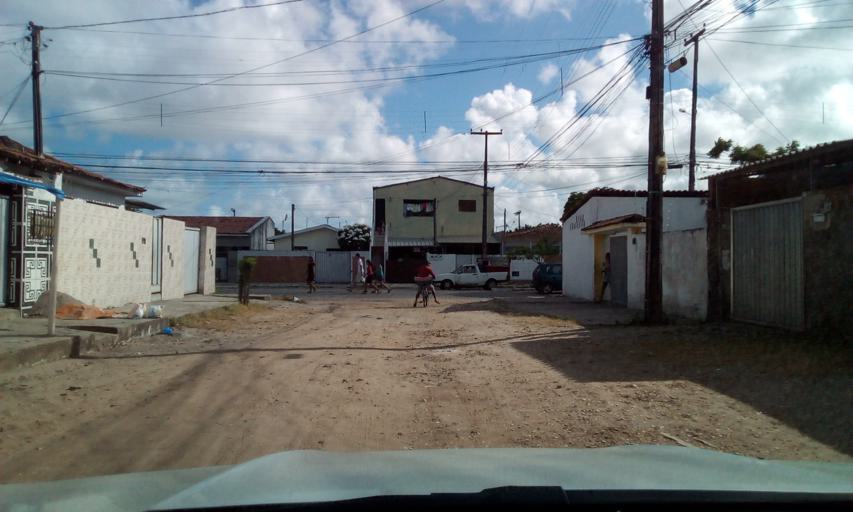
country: BR
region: Paraiba
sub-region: Joao Pessoa
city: Joao Pessoa
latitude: -7.1683
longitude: -34.8348
